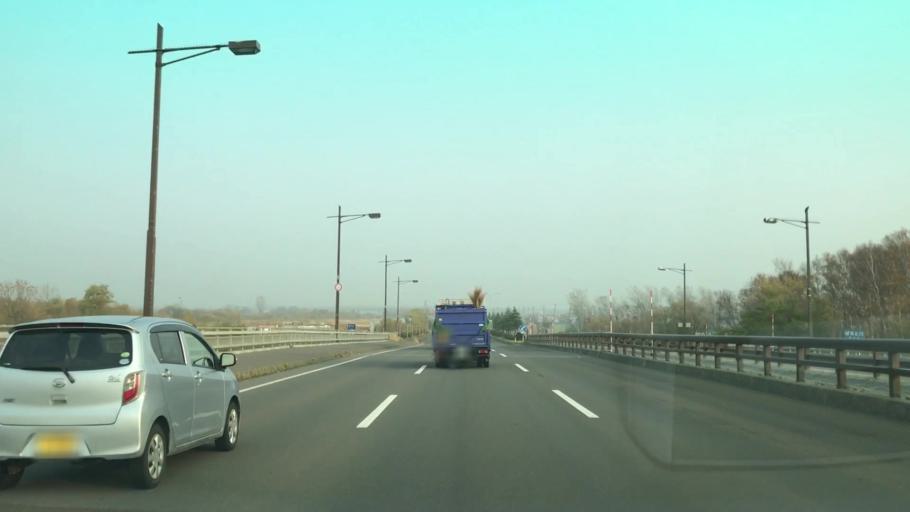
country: JP
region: Hokkaido
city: Ishikari
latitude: 43.1686
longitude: 141.3484
